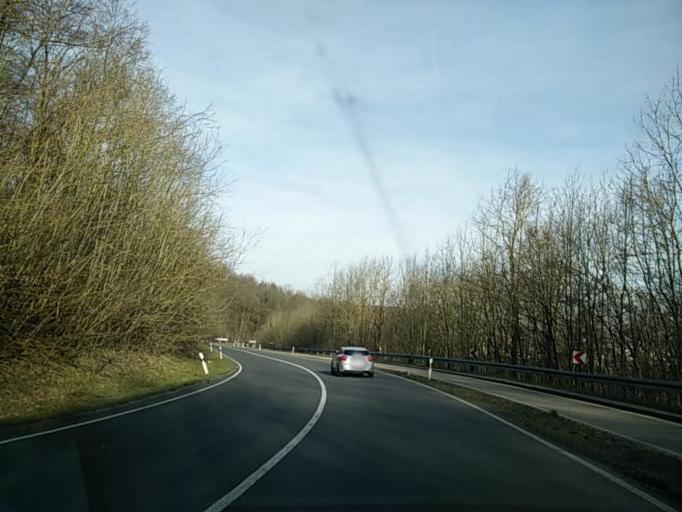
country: DE
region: Baden-Wuerttemberg
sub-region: Regierungsbezirk Stuttgart
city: Boeblingen
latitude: 48.6613
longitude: 9.0085
